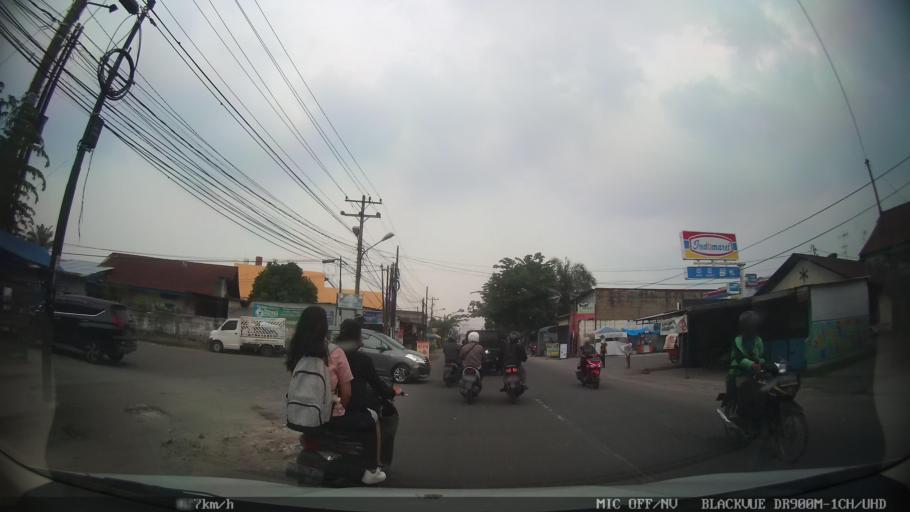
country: ID
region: North Sumatra
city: Deli Tua
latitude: 3.5532
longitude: 98.7161
